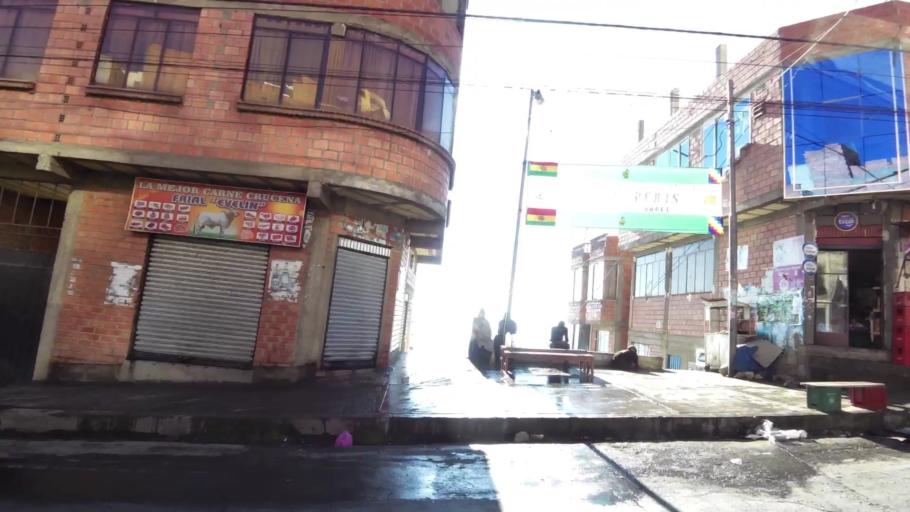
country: BO
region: La Paz
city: La Paz
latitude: -16.5067
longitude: -68.1526
